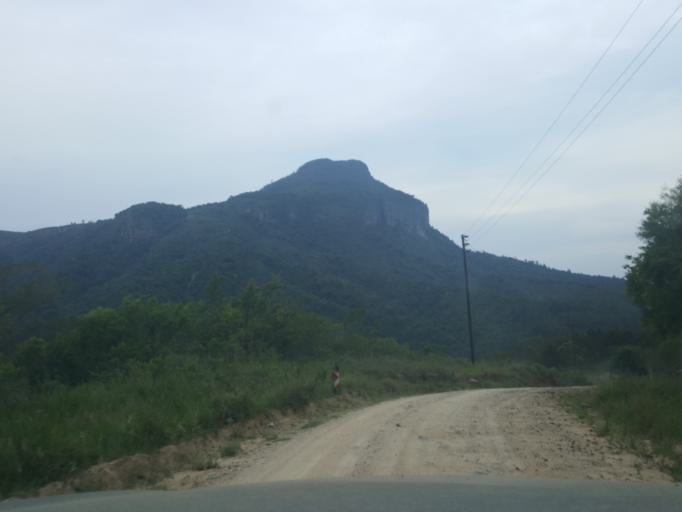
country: ZA
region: Limpopo
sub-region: Mopani District Municipality
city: Hoedspruit
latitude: -24.5956
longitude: 30.8758
